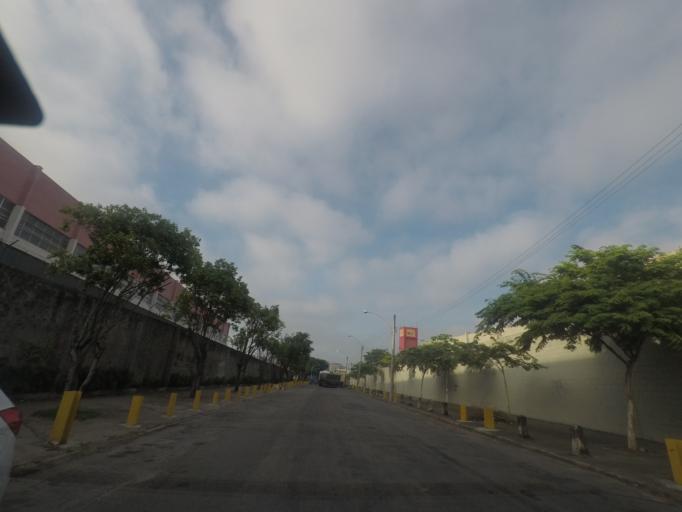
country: BR
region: Rio de Janeiro
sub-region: Duque De Caxias
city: Duque de Caxias
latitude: -22.8356
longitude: -43.2625
